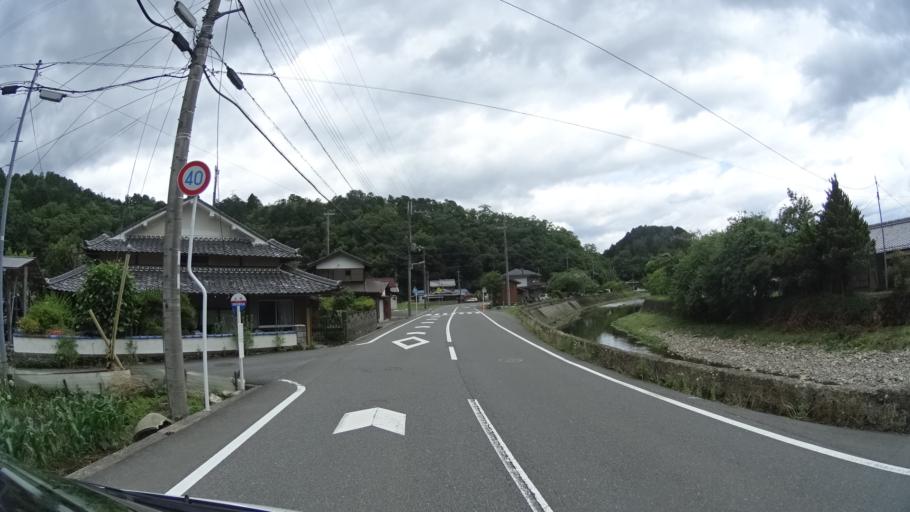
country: JP
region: Kyoto
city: Kameoka
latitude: 35.0915
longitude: 135.4211
